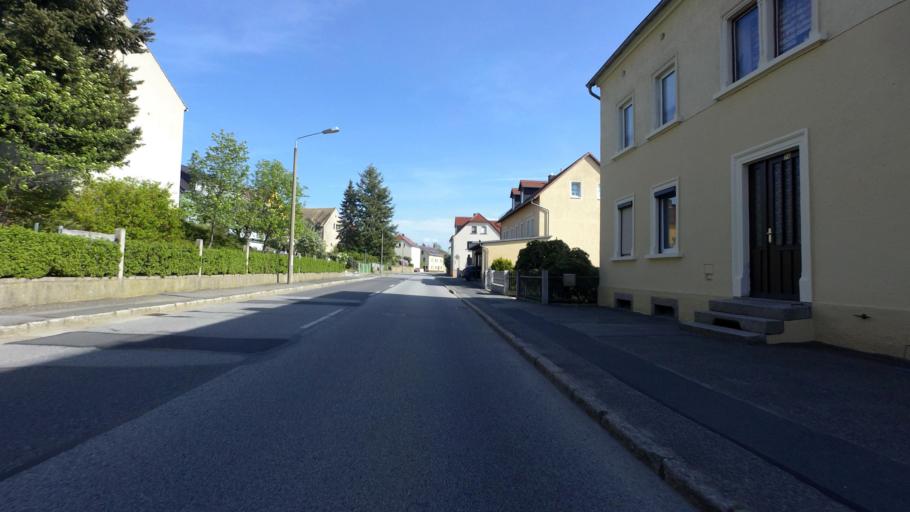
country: DE
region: Saxony
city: Kamenz
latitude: 51.2588
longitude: 14.1163
